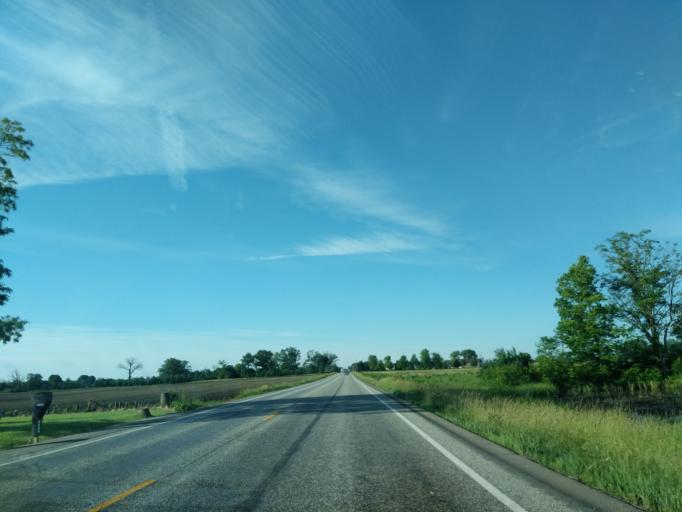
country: US
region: Indiana
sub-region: Madison County
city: Ingalls
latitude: 39.9233
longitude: -85.7711
